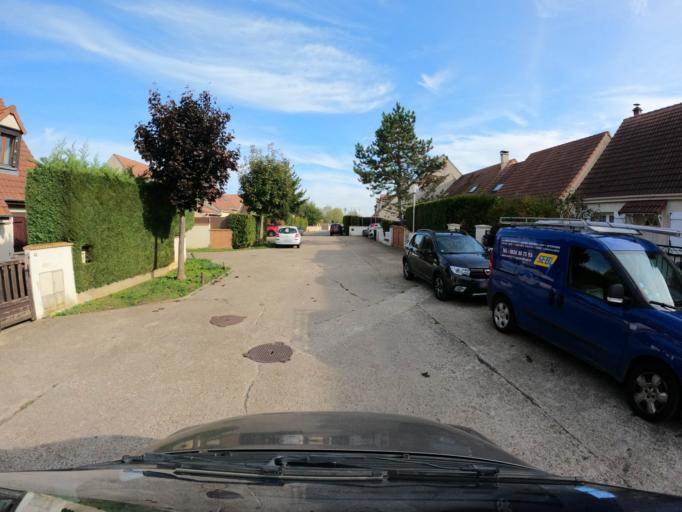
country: FR
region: Ile-de-France
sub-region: Departement du Val-de-Marne
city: La Queue-en-Brie
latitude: 48.7798
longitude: 2.5918
